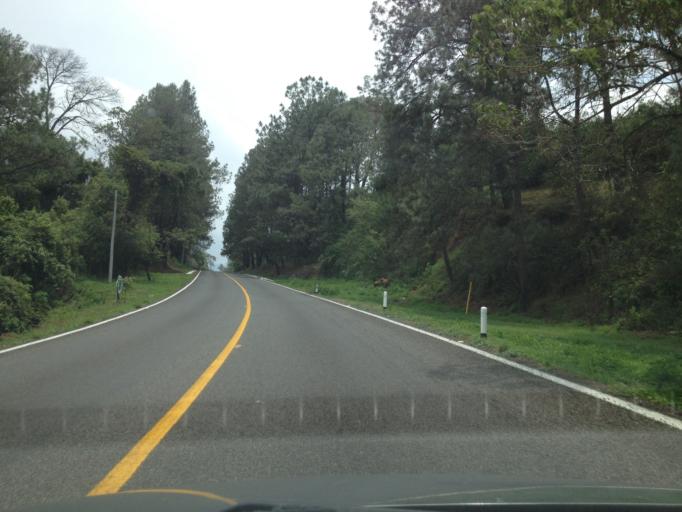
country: MX
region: Michoacan
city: Tingambato
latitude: 19.4761
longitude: -101.9284
